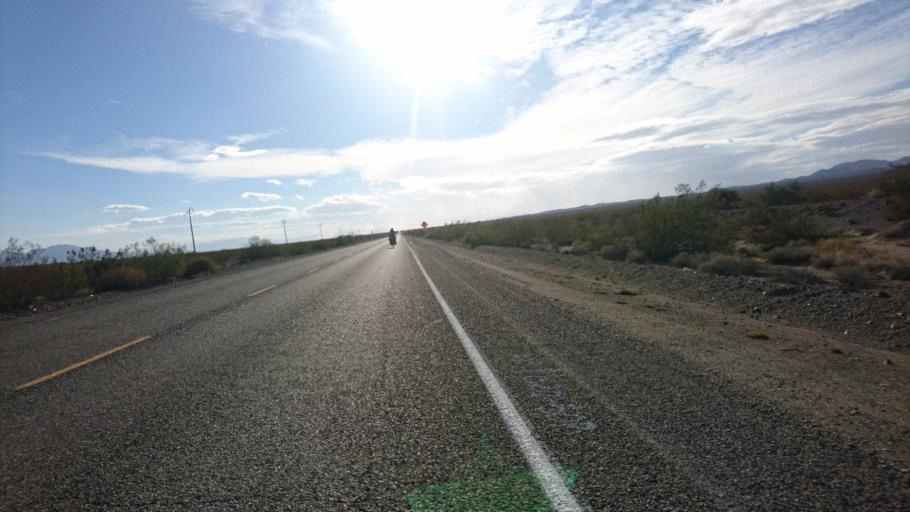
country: US
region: California
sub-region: San Bernardino County
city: Needles
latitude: 34.6929
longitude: -115.3086
